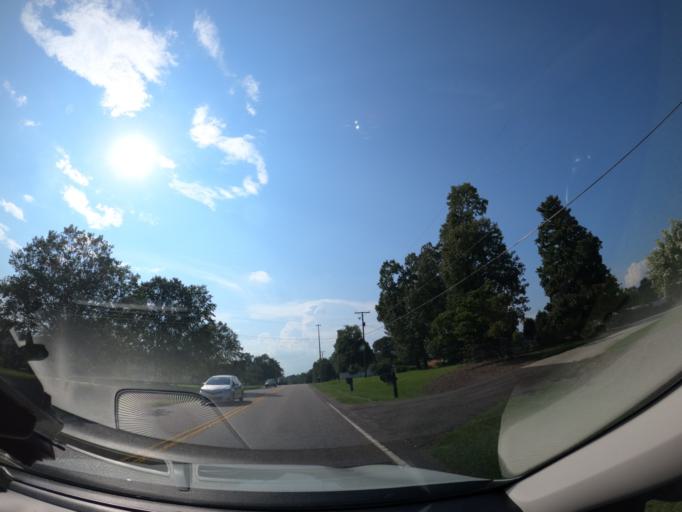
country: US
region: South Carolina
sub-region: Aiken County
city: Clearwater
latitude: 33.4179
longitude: -81.8482
